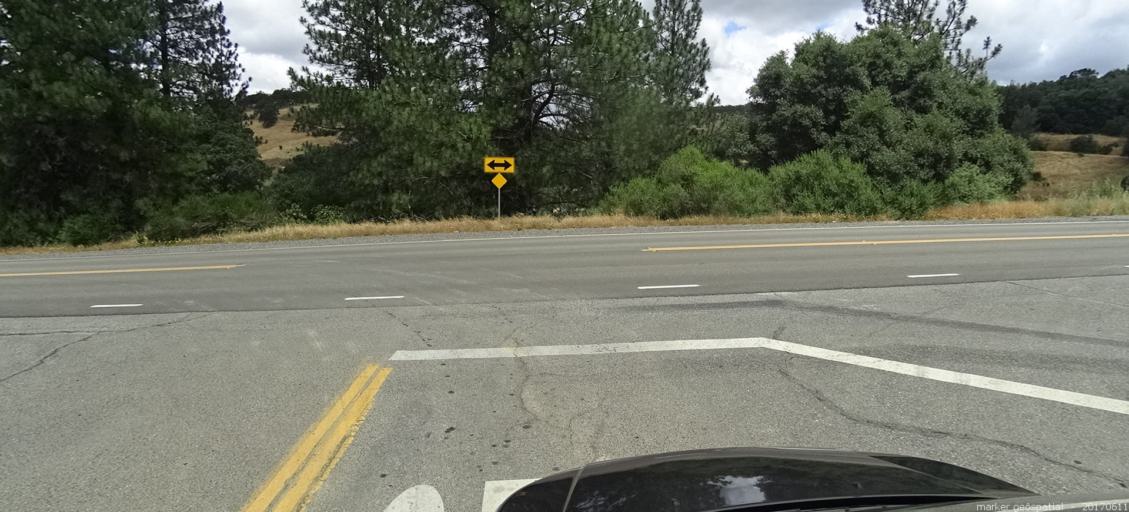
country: US
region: California
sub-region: Butte County
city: Paradise
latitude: 39.6530
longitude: -121.5515
